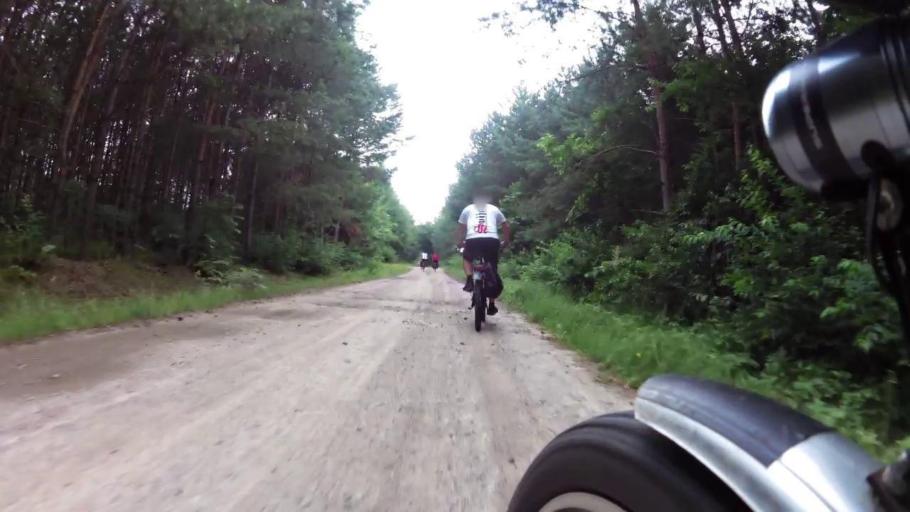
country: PL
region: West Pomeranian Voivodeship
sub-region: Powiat gryfinski
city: Mieszkowice
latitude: 52.8360
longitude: 14.5940
